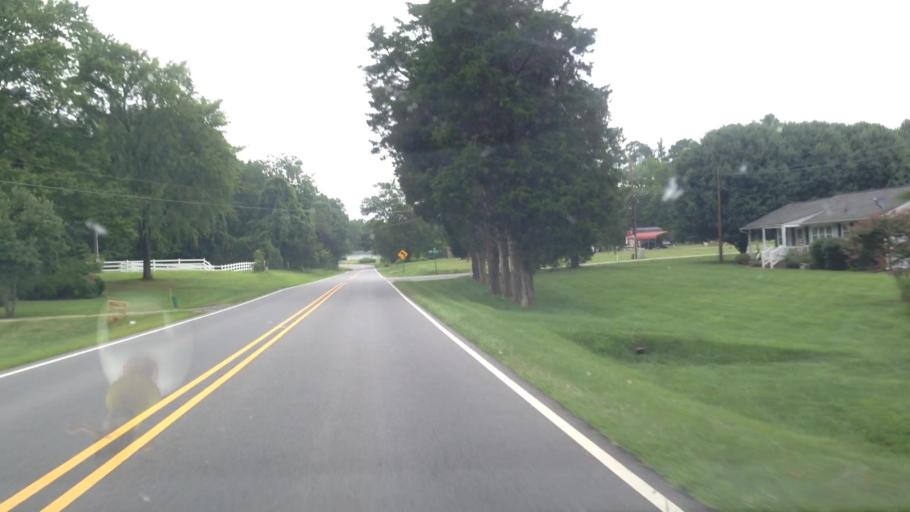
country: US
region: North Carolina
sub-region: Rockingham County
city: Mayodan
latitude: 36.4113
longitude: -80.0058
